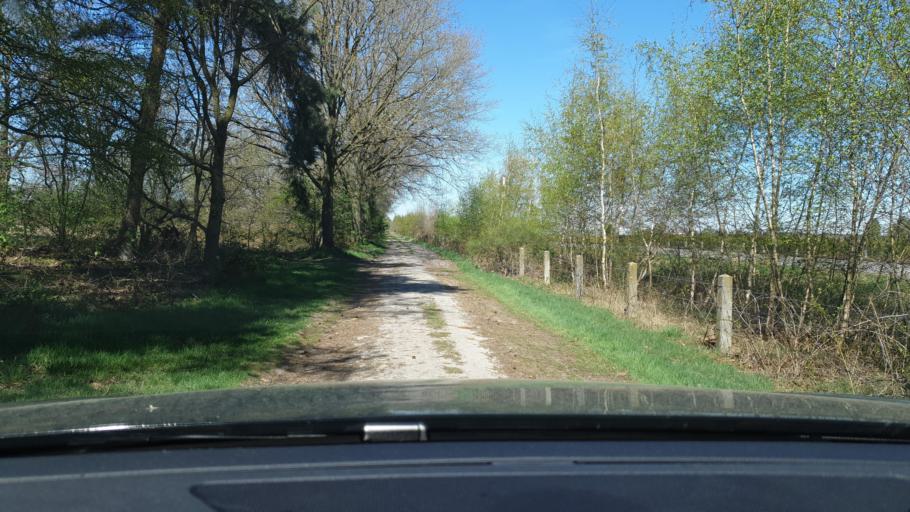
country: NL
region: Limburg
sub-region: Gemeente Venlo
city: Arcen
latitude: 51.4520
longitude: 6.1191
